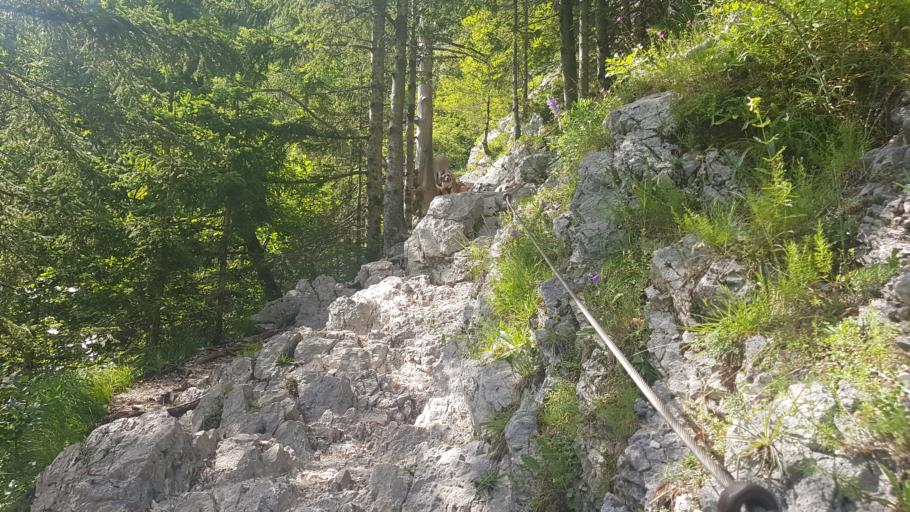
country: SI
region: Kranjska Gora
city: Kranjska Gora
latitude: 46.4114
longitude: 13.7244
